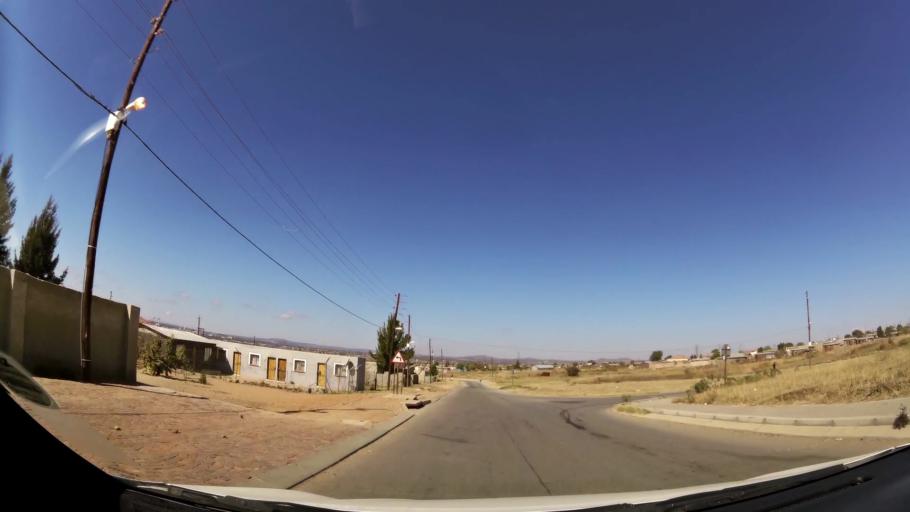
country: ZA
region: Limpopo
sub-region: Capricorn District Municipality
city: Polokwane
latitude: -23.8850
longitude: 29.4091
